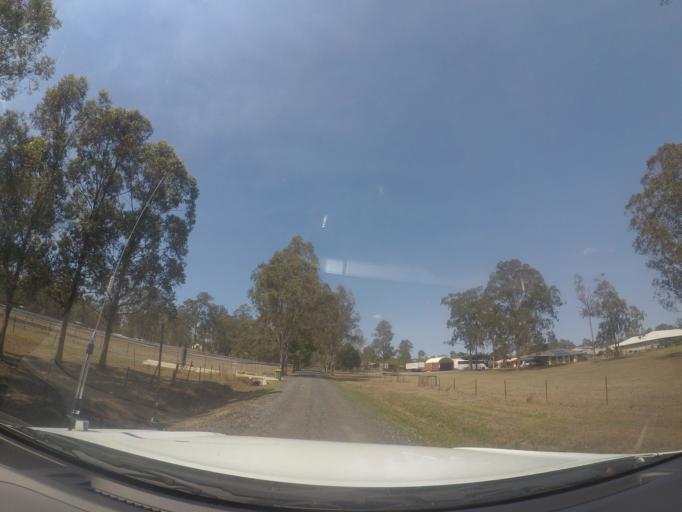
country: AU
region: Queensland
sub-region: Logan
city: North Maclean
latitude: -27.7867
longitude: 153.0279
